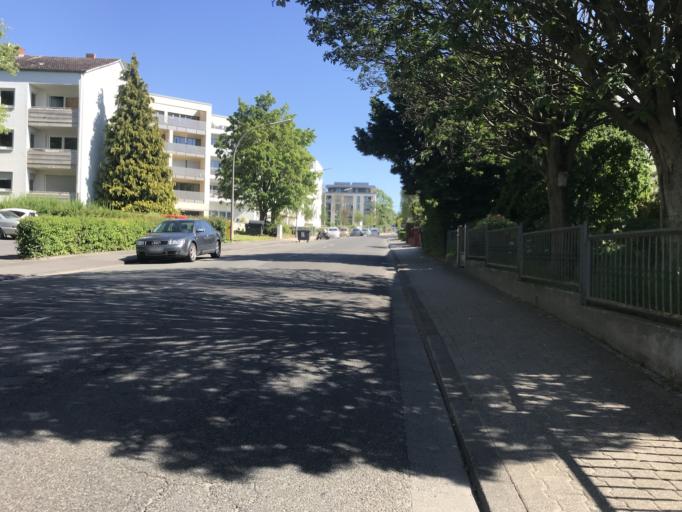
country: DE
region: Hesse
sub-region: Regierungsbezirk Darmstadt
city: Walluf
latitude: 50.0531
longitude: 8.1975
